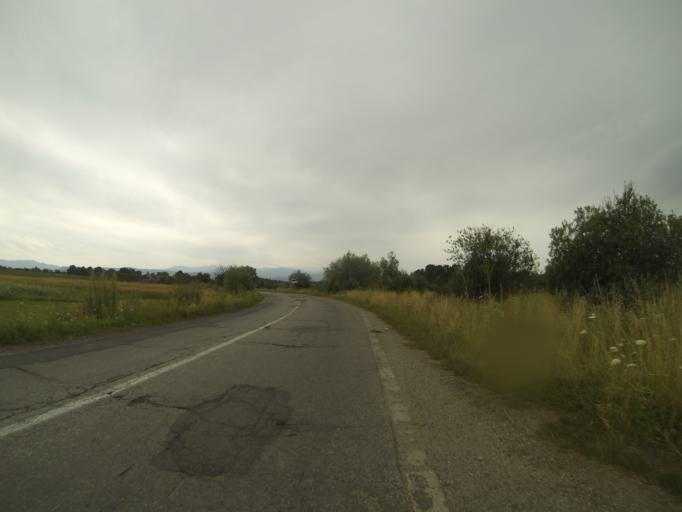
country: RO
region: Brasov
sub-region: Comuna Sinca Veche
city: Sinca Veche
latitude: 45.7755
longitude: 25.1488
